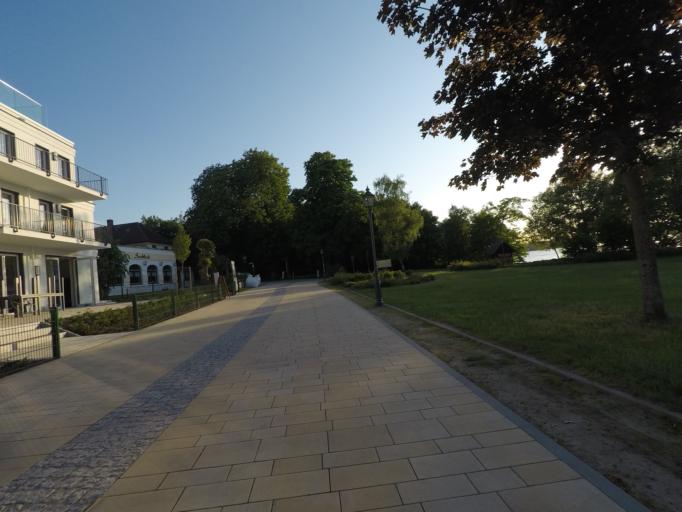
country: DE
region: Brandenburg
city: Joachimsthal
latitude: 52.9136
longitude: 13.7083
